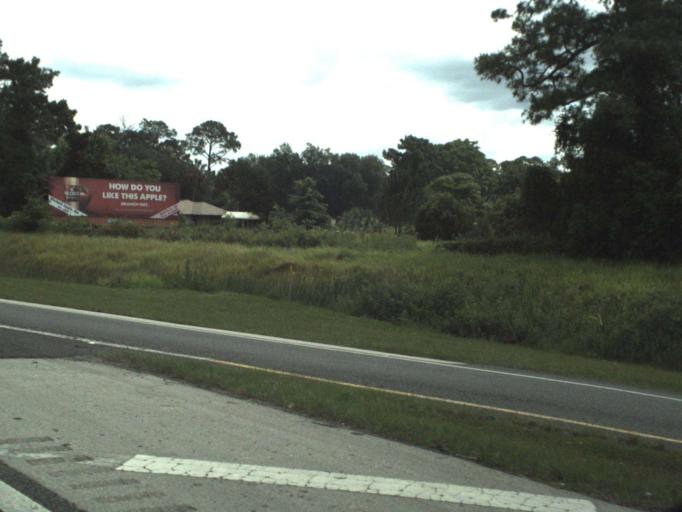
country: US
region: Florida
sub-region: Volusia County
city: Lake Helen
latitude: 28.9882
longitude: -81.2470
